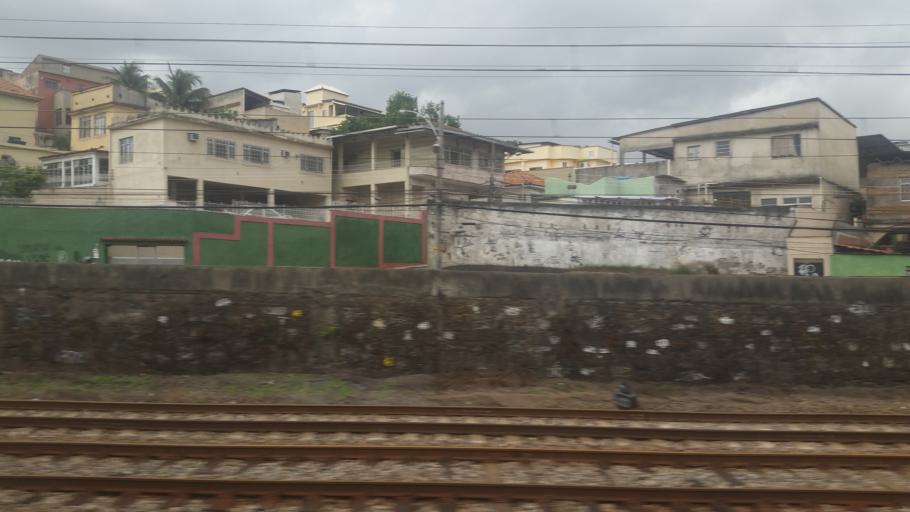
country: BR
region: Rio de Janeiro
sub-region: Sao Joao De Meriti
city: Sao Joao de Meriti
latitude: -22.8889
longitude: -43.3151
